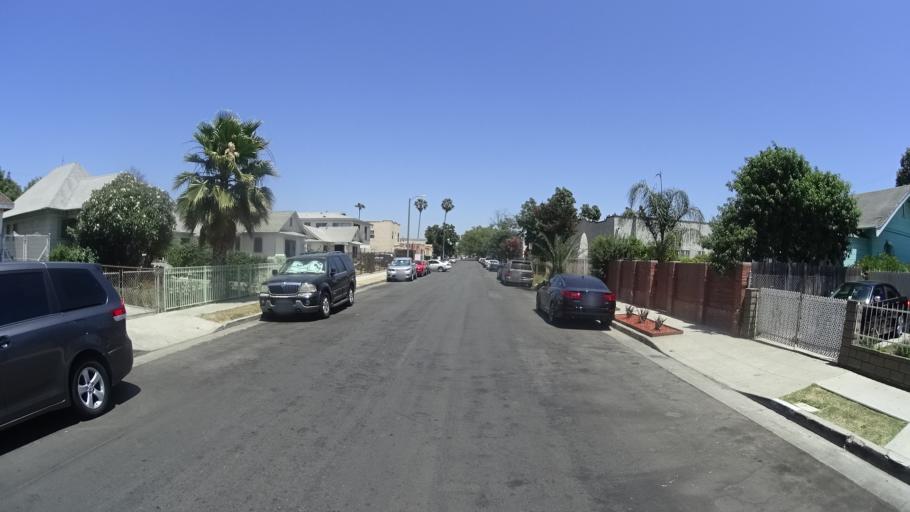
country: US
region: California
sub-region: Los Angeles County
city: View Park-Windsor Hills
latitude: 34.0173
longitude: -118.2975
